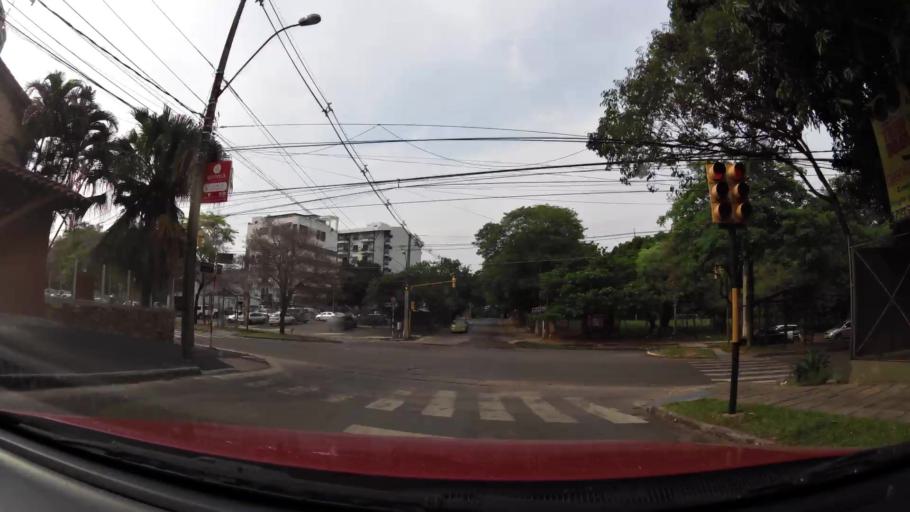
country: PY
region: Central
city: Fernando de la Mora
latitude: -25.2884
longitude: -57.5556
